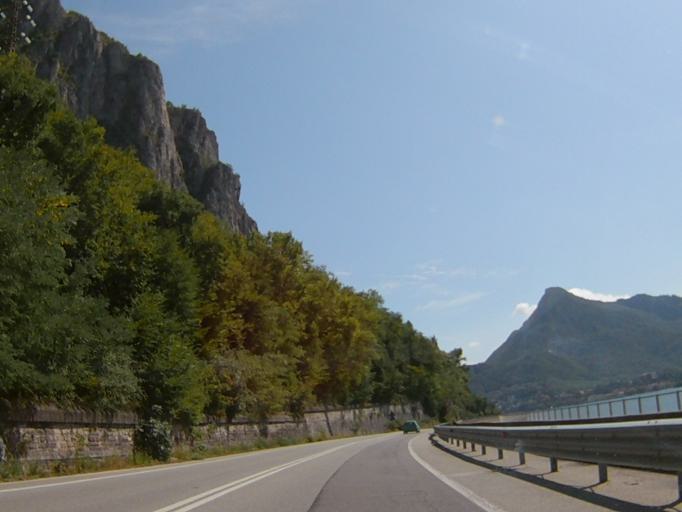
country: IT
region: Lombardy
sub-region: Provincia di Lecco
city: Lecco
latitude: 45.8743
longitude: 9.3773
